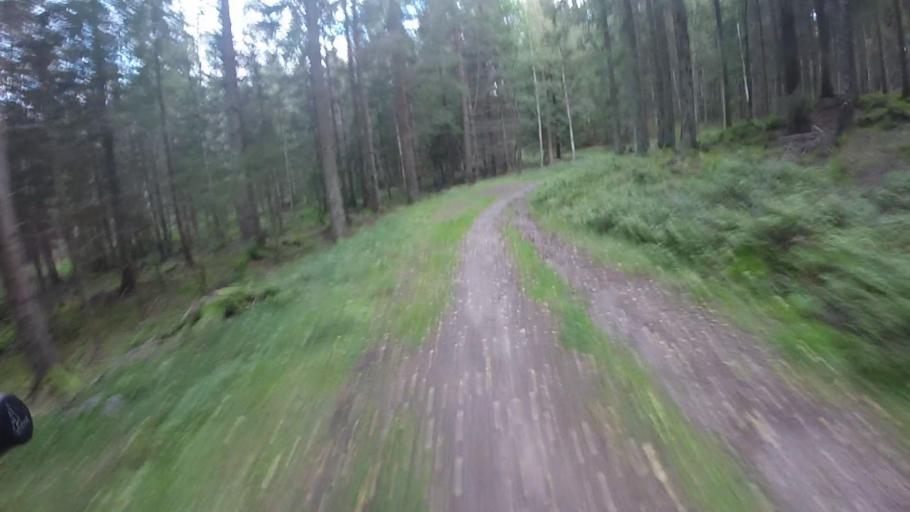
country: SE
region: Vaestra Goetaland
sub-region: Trollhattan
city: Trollhattan
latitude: 58.2559
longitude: 12.2390
